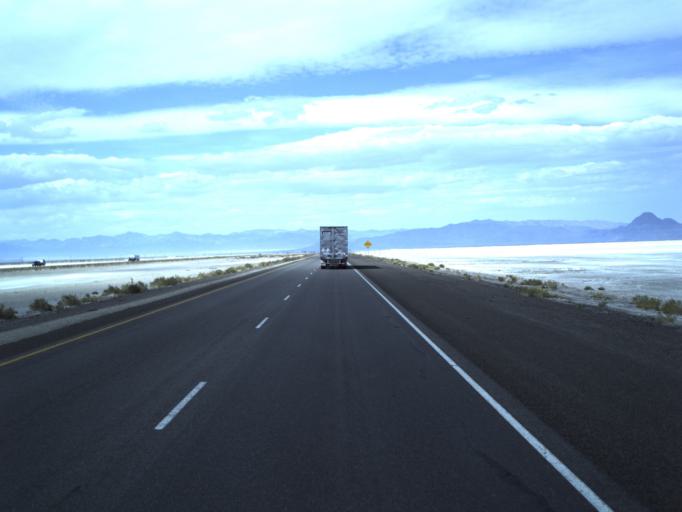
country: US
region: Utah
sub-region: Tooele County
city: Wendover
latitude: 40.7379
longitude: -113.7772
